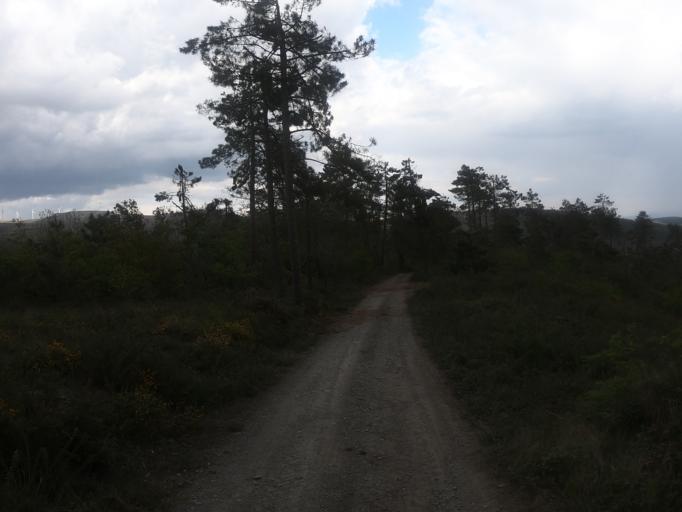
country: PT
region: Vila Real
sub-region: Mondim de Basto
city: Mondim de Basto
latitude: 41.3113
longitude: -7.8885
